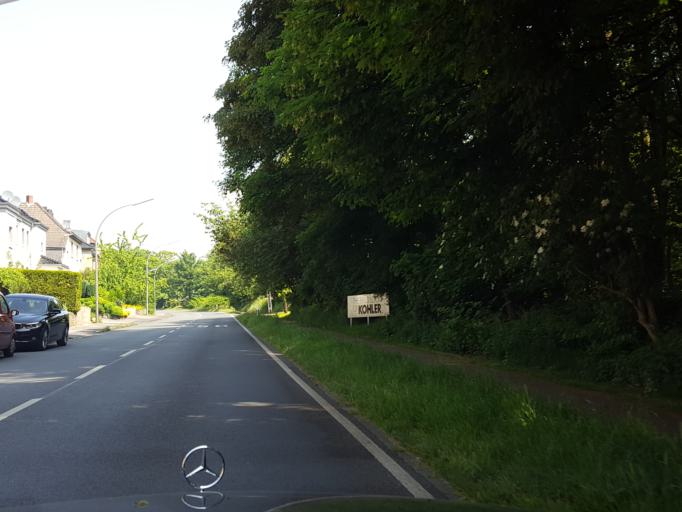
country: DE
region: North Rhine-Westphalia
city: Oer-Erkenschwick
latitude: 51.6481
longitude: 7.2772
